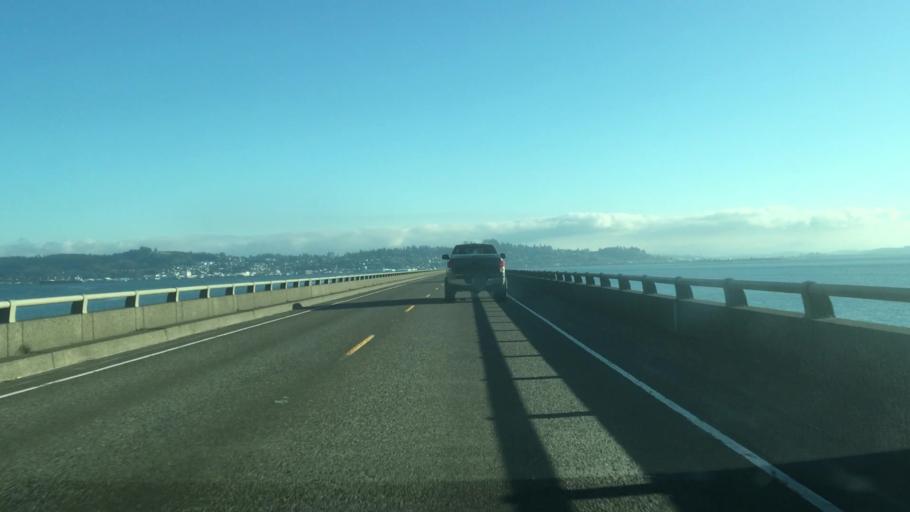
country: US
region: Oregon
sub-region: Clatsop County
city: Astoria
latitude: 46.2246
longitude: -123.8667
